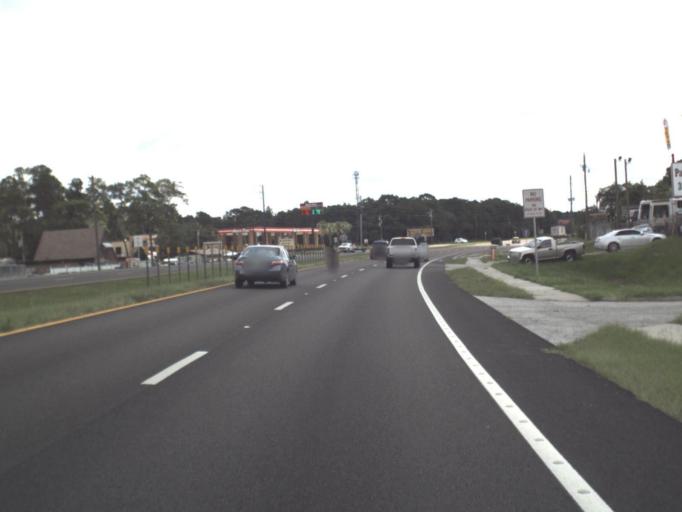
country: US
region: Florida
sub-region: Hernando County
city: Brookridge
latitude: 28.5403
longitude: -82.4651
